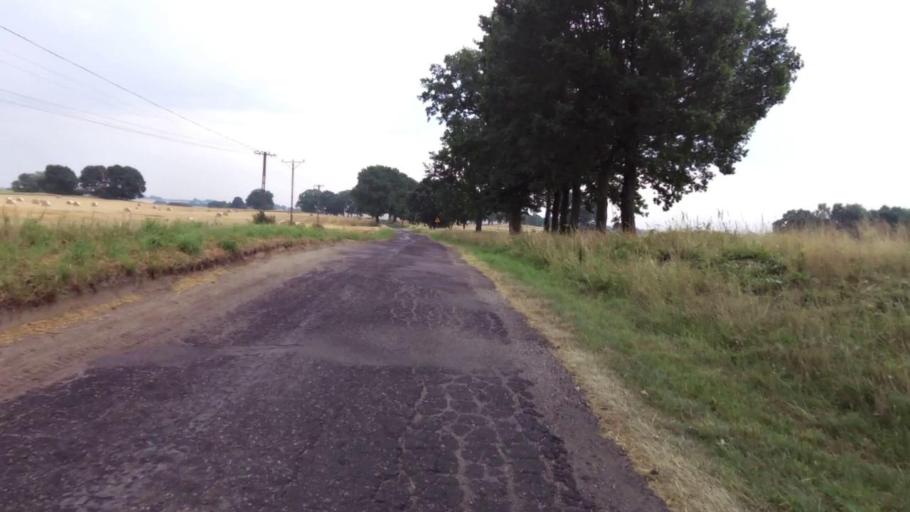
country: PL
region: West Pomeranian Voivodeship
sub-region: Powiat drawski
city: Drawsko Pomorskie
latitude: 53.5355
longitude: 15.7360
